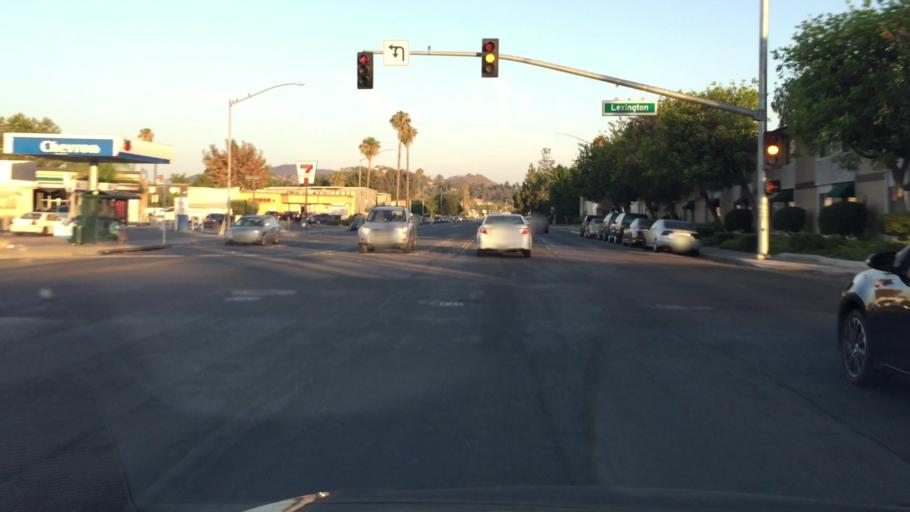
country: US
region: California
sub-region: San Diego County
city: Bostonia
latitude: 32.7926
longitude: -116.9337
